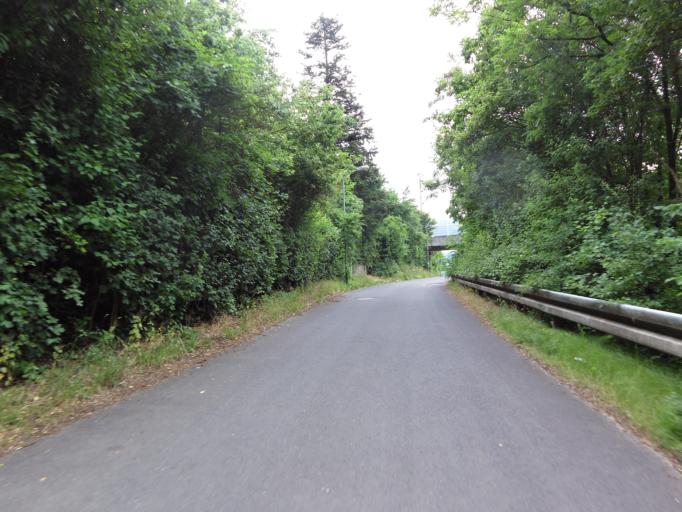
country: DE
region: Bavaria
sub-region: Regierungsbezirk Unterfranken
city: Veitshochheim
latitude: 49.8226
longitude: 9.8789
